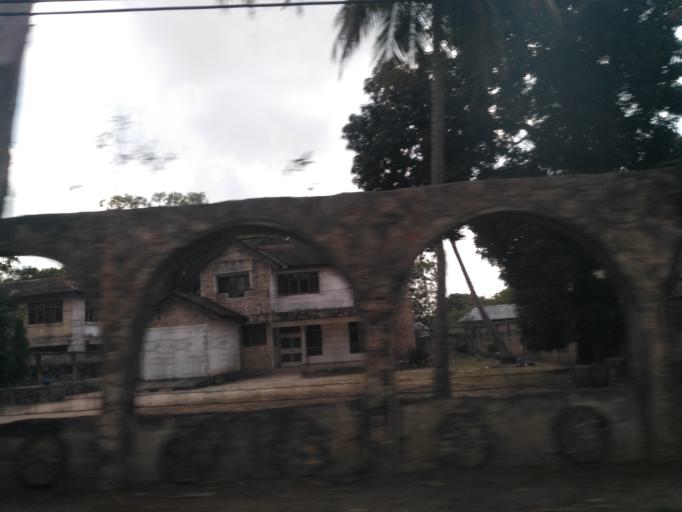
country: TZ
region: Dar es Salaam
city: Magomeni
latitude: -6.7459
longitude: 39.2361
